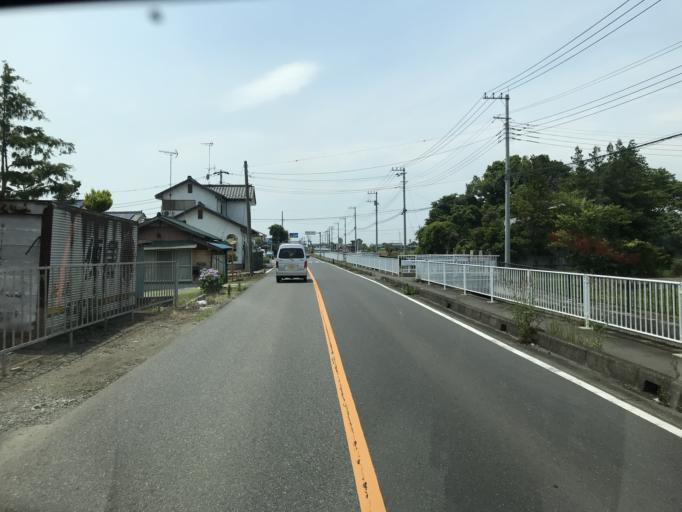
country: JP
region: Saitama
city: Satte
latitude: 36.0747
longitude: 139.7510
